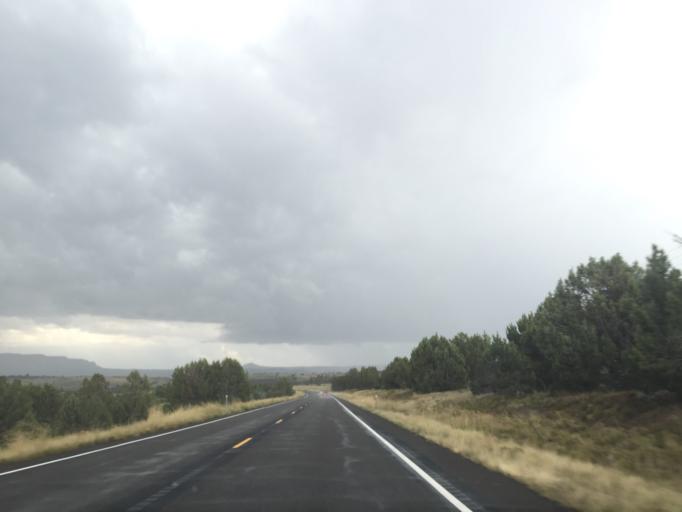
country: US
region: Utah
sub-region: Kane County
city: Kanab
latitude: 37.2420
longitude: -112.7517
